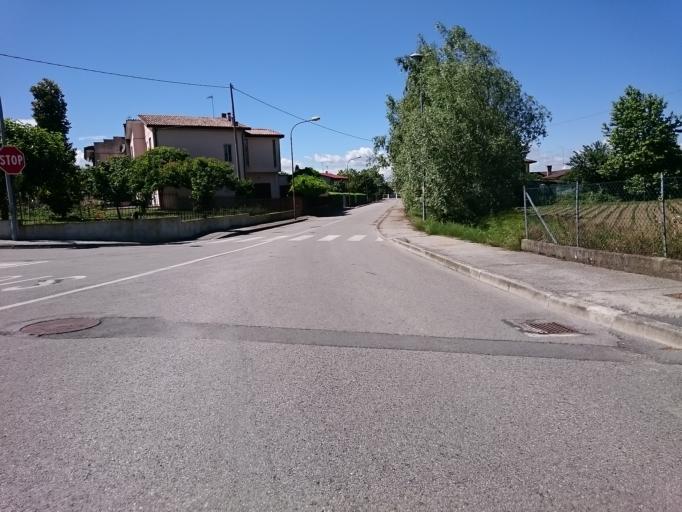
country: IT
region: Veneto
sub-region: Provincia di Padova
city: Vallonga
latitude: 45.2701
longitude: 12.0823
